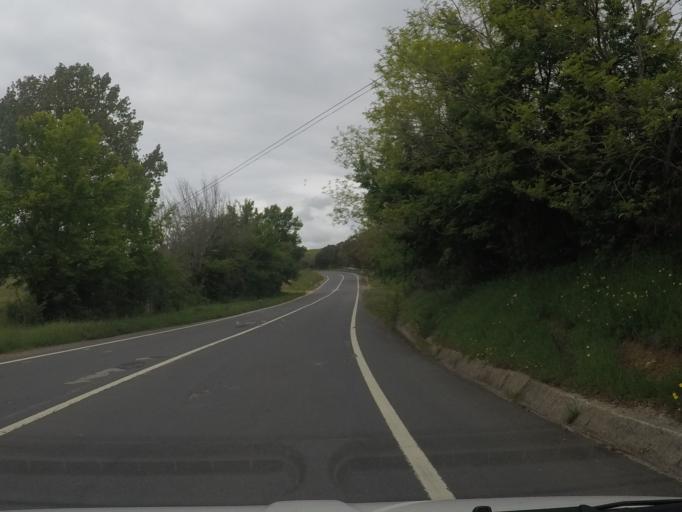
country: PT
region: Setubal
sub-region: Santiago do Cacem
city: Cercal
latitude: 37.8274
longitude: -8.6974
